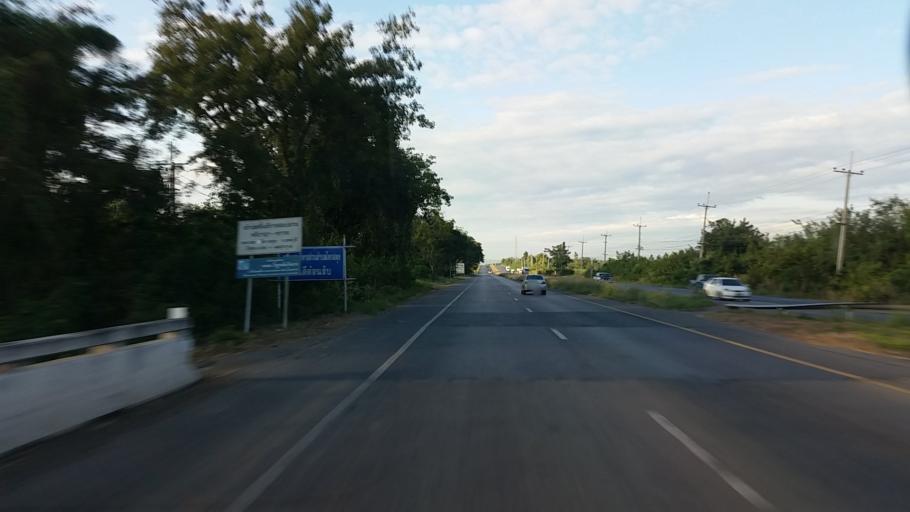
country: TH
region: Lop Buri
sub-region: Amphoe Tha Luang
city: Tha Luang
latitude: 15.0565
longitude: 100.9695
